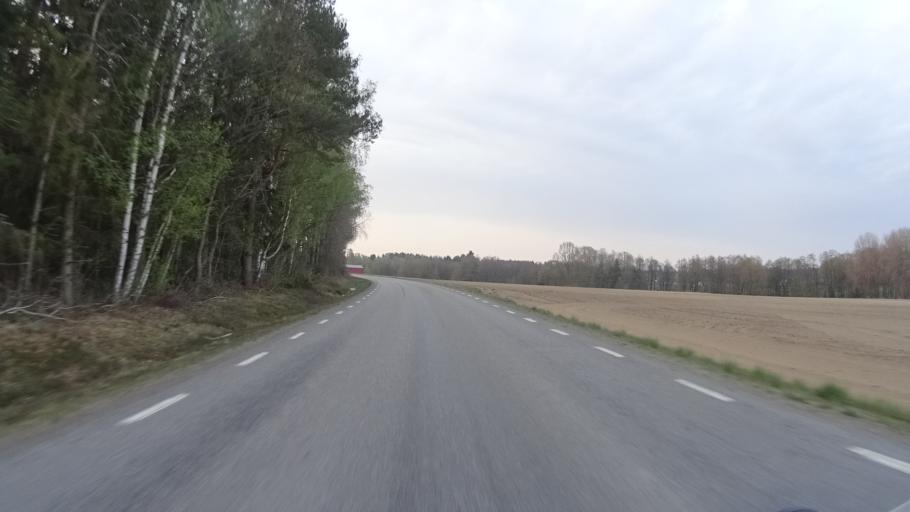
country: SE
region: Vaestra Goetaland
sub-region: Lidkopings Kommun
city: Vinninga
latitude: 58.4339
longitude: 13.3398
